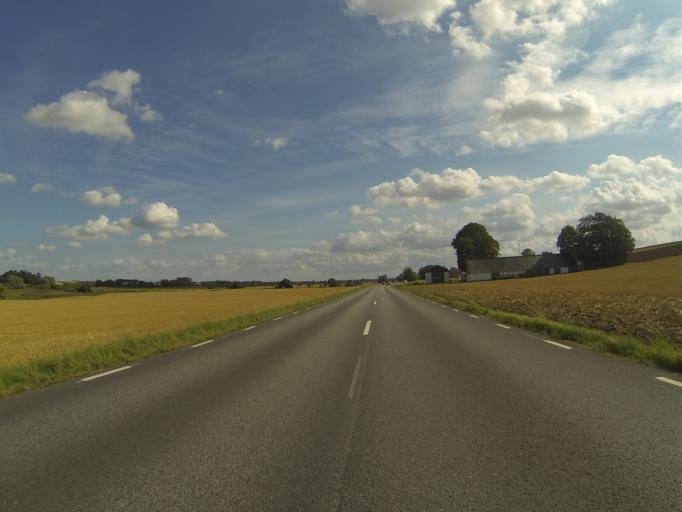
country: SE
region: Skane
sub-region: Eslovs Kommun
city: Eslov
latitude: 55.7592
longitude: 13.3167
